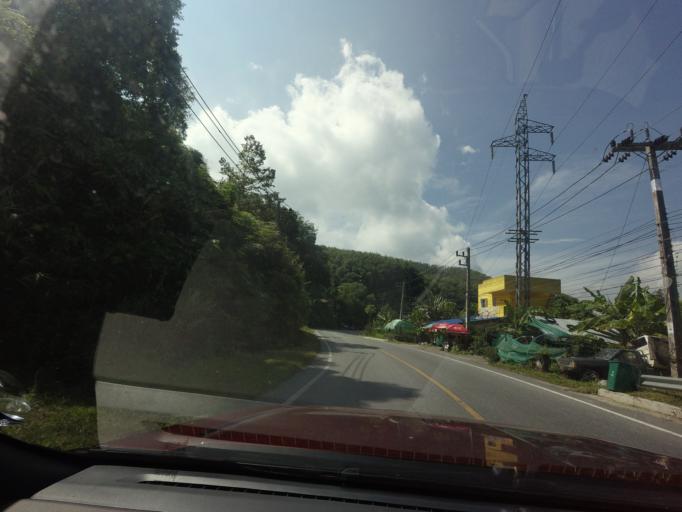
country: TH
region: Yala
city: Betong
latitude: 5.9002
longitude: 101.1453
